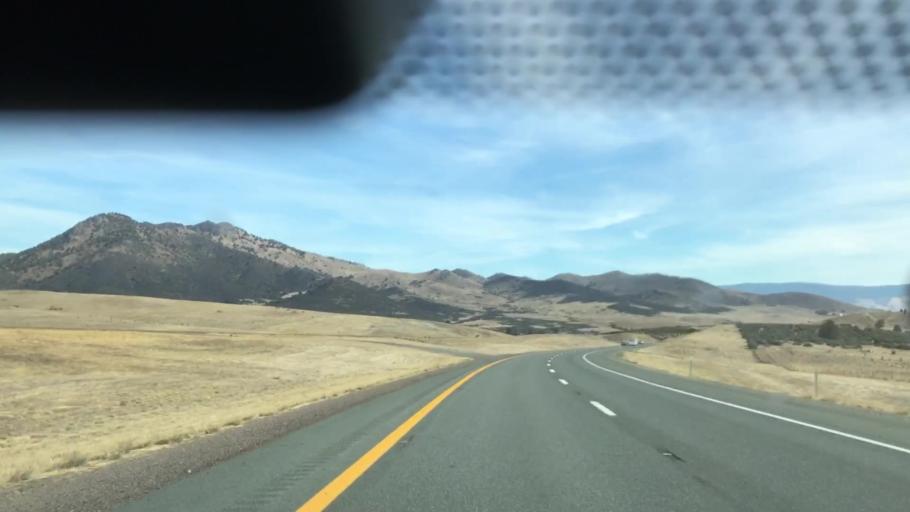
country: US
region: California
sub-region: Siskiyou County
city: Yreka
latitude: 41.7588
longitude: -122.5962
